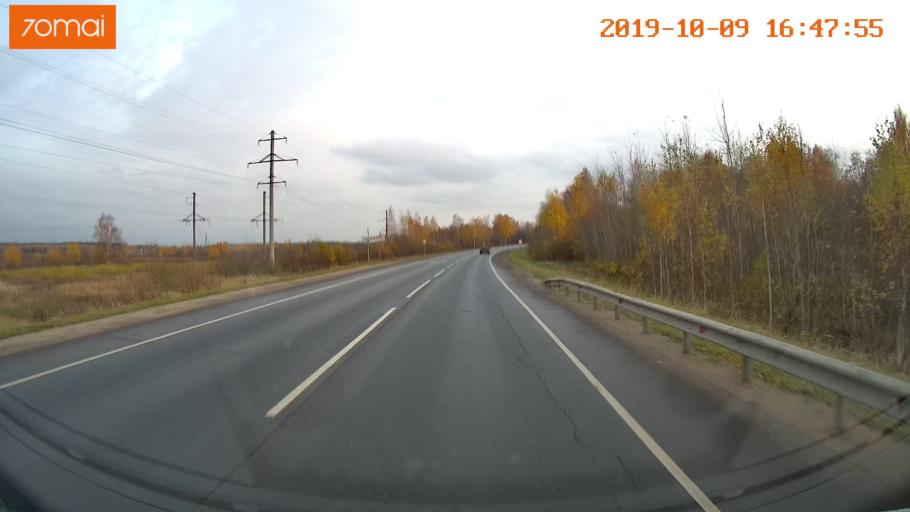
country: RU
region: Kostroma
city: Volgorechensk
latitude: 57.4334
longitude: 41.1849
